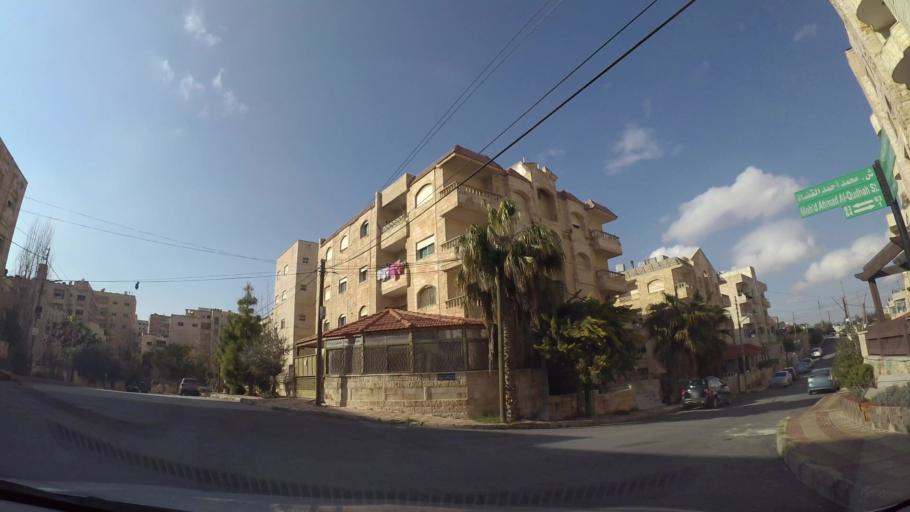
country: JO
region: Amman
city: Al Jubayhah
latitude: 32.0201
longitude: 35.8587
